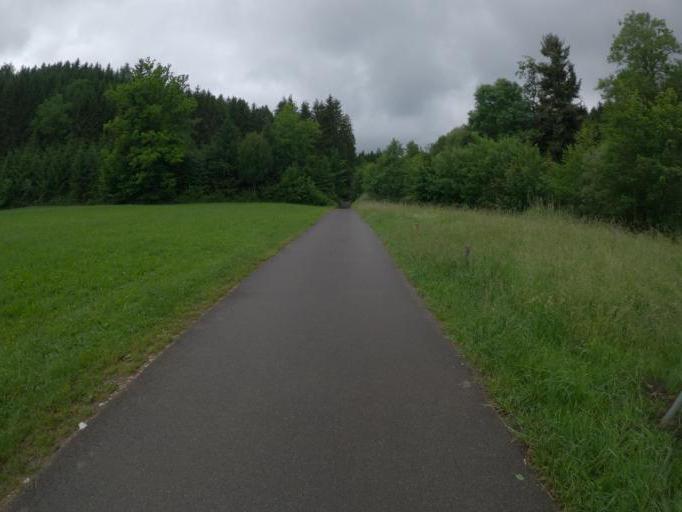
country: DE
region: Baden-Wuerttemberg
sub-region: Regierungsbezirk Stuttgart
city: Bortlingen
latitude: 48.7439
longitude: 9.6201
